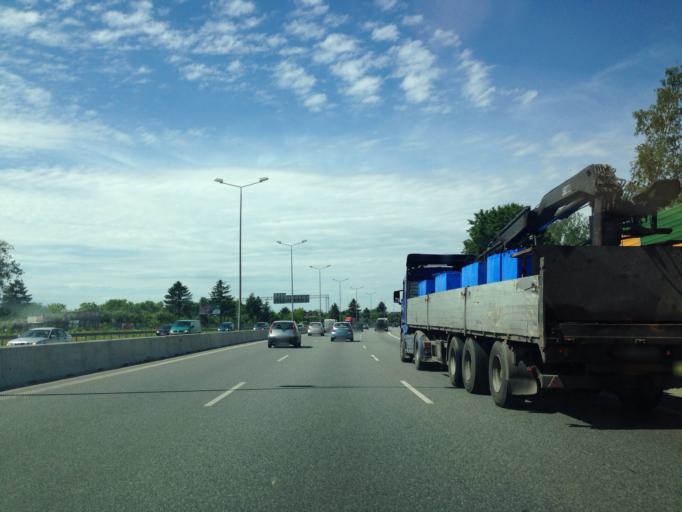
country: PL
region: Masovian Voivodeship
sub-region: Warszawa
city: Bemowo
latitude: 52.2497
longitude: 20.9372
